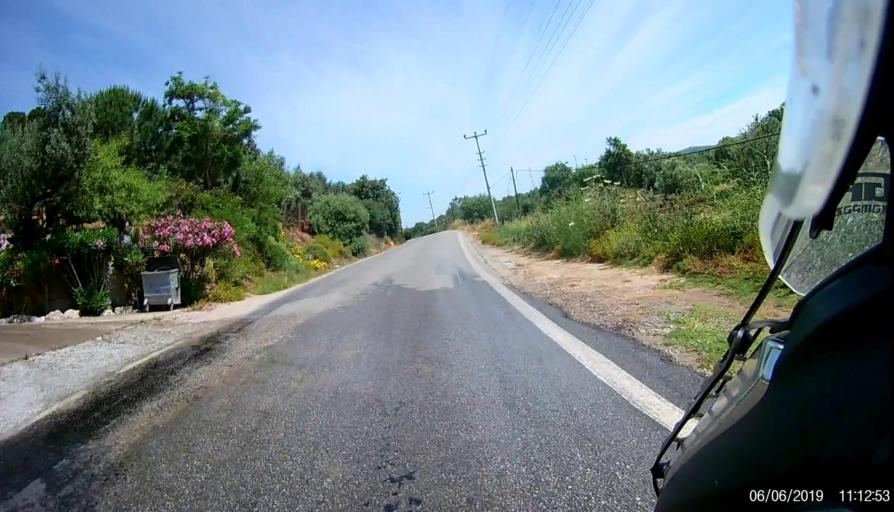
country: TR
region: Canakkale
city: Gulpinar
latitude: 39.6124
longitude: 26.1826
